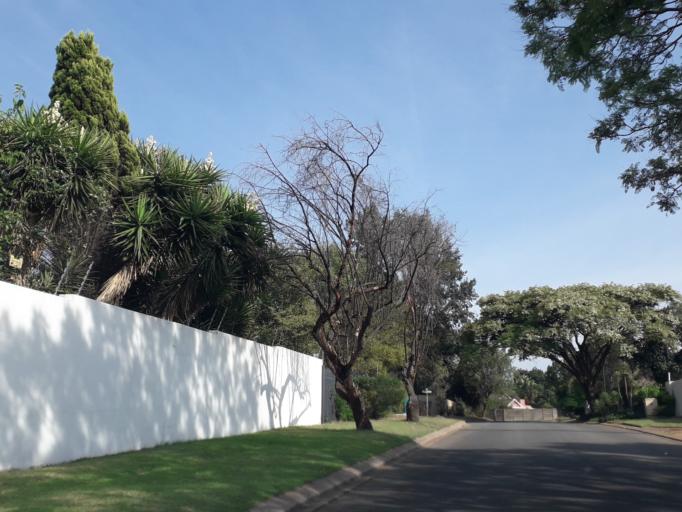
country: ZA
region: Gauteng
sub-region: City of Johannesburg Metropolitan Municipality
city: Diepsloot
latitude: -26.0337
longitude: 28.0212
